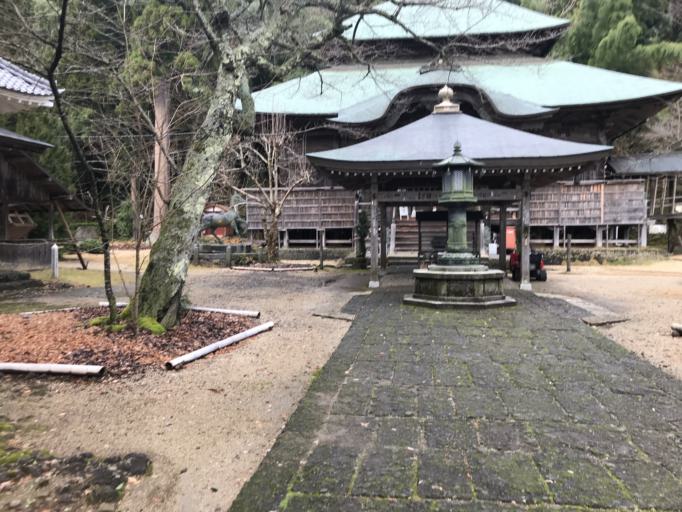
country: JP
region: Kyoto
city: Maizuru
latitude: 35.4971
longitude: 135.4692
